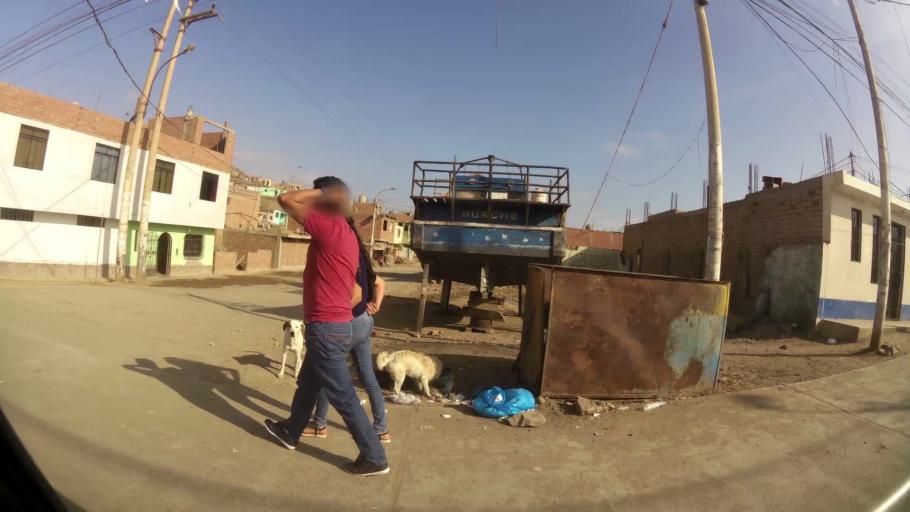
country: PE
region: Lima
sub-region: Huaura
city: Huacho
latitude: -11.1278
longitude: -77.6163
